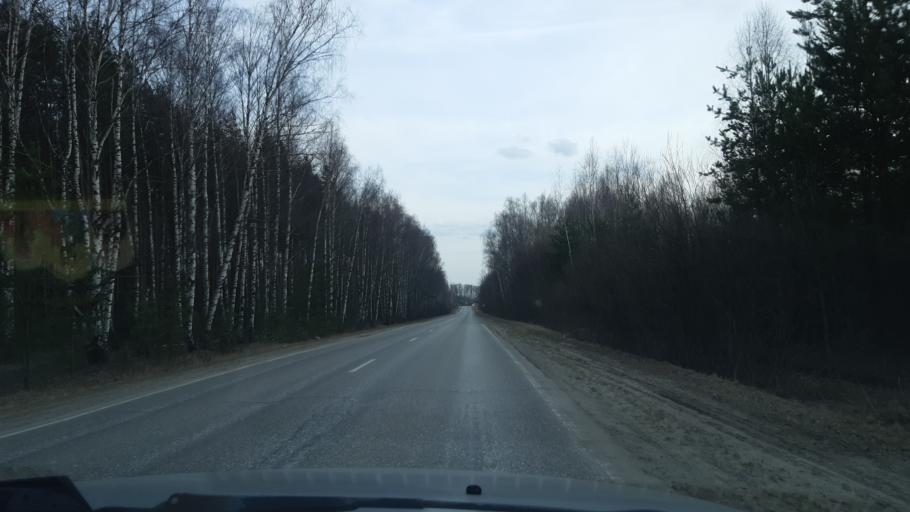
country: RU
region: Vladimir
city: Luknovo
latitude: 56.2289
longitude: 42.0346
